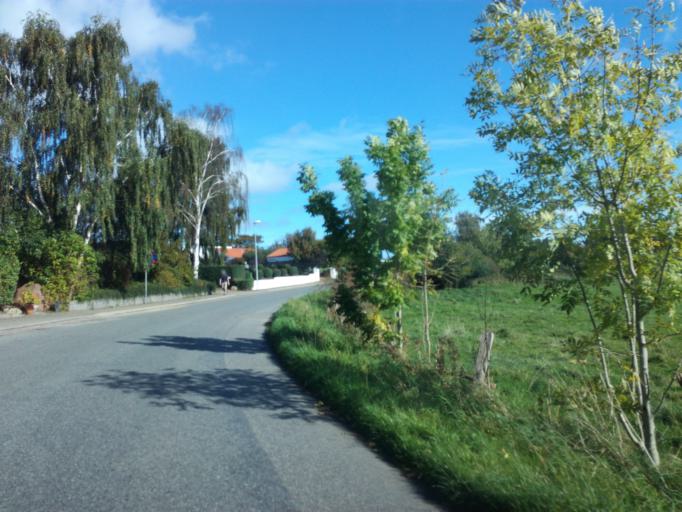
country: DK
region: South Denmark
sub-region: Fredericia Kommune
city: Fredericia
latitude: 55.6232
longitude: 9.7852
